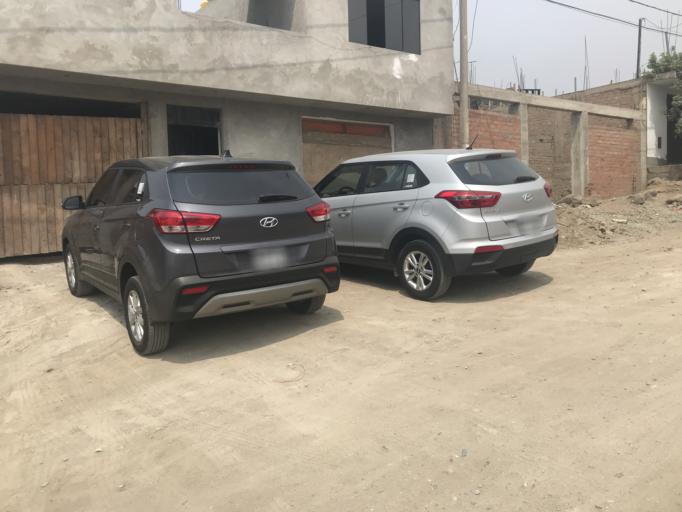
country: PE
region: Lima
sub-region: Lima
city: Carabayllo
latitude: -11.8183
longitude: -77.0436
